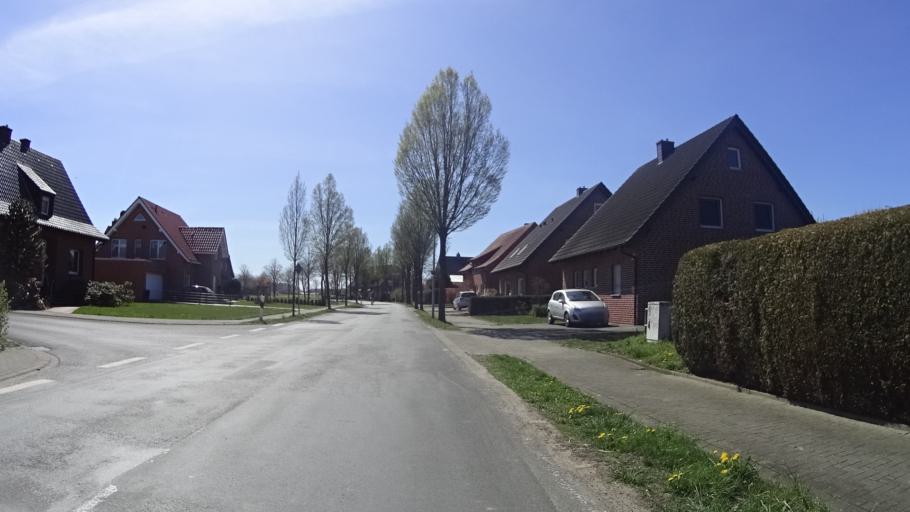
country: DE
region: North Rhine-Westphalia
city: Ludinghausen
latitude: 51.8322
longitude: 7.4000
